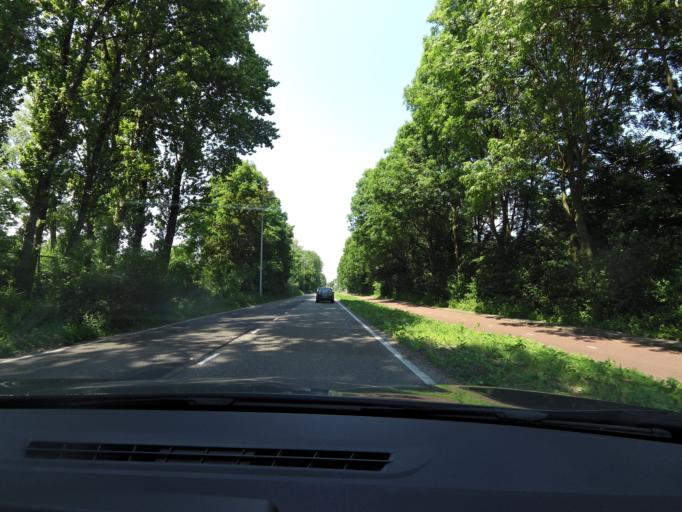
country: NL
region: South Holland
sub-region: Gemeente Rotterdam
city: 's-Gravenland
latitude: 51.9342
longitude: 4.5320
